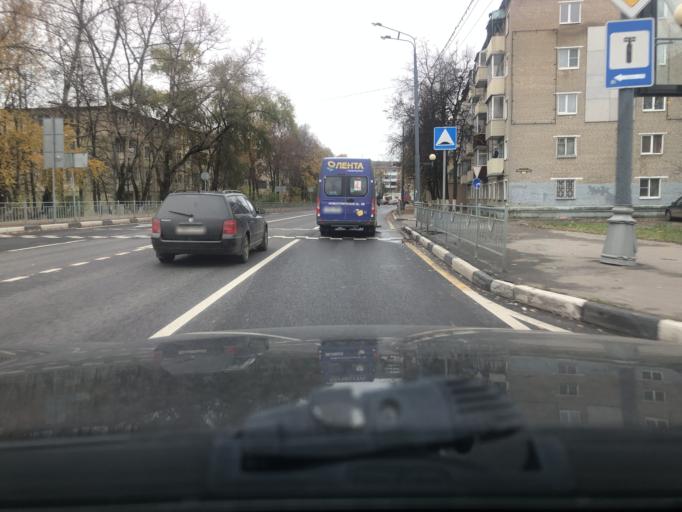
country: RU
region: Moskovskaya
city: Sergiyev Posad
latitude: 56.3211
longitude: 38.1380
